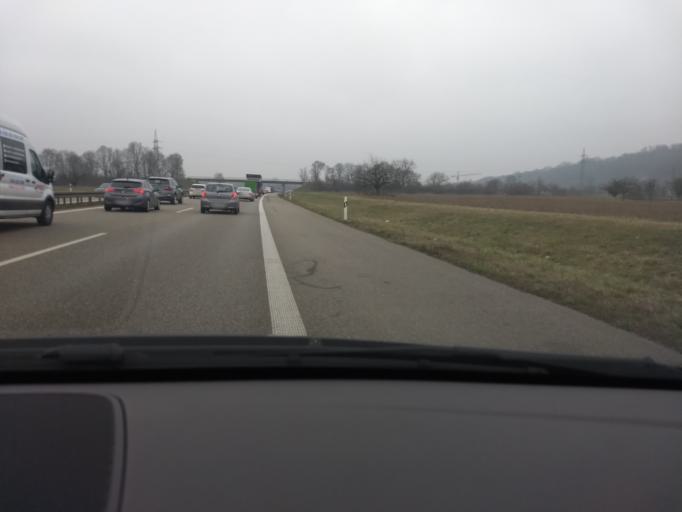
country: FR
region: Alsace
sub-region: Departement du Haut-Rhin
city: Kembs
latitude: 47.6943
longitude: 7.5207
